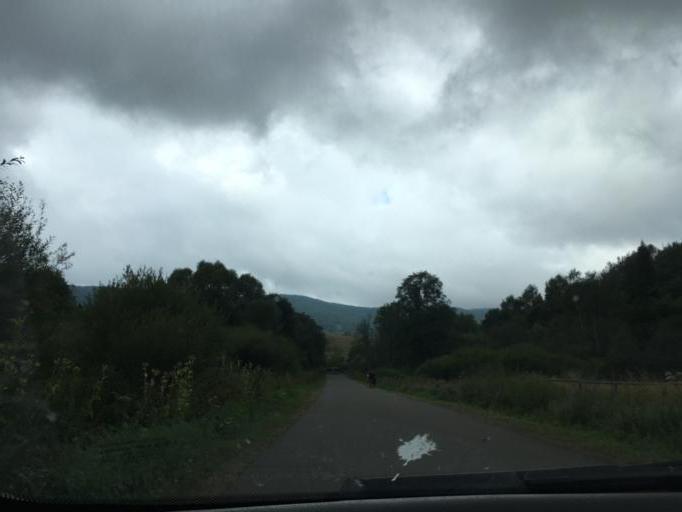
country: PL
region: Subcarpathian Voivodeship
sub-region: Powiat bieszczadzki
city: Lutowiska
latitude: 49.1438
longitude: 22.5702
